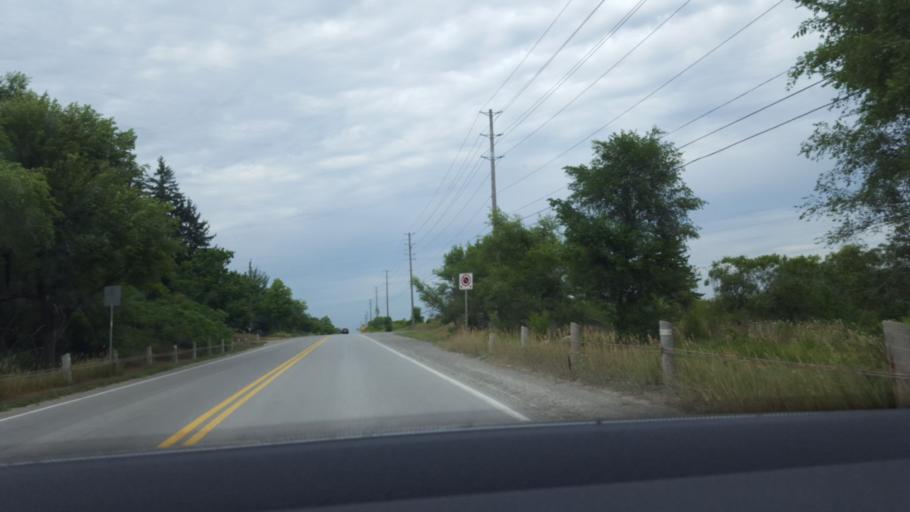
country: CA
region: Ontario
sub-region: Halton
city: Milton
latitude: 43.5035
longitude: -79.9627
